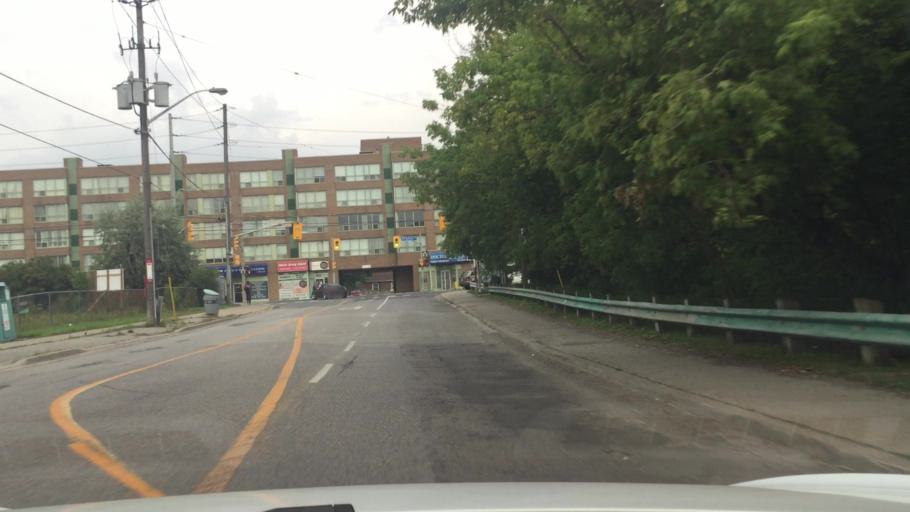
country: CA
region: Ontario
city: Scarborough
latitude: 43.7083
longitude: -79.3119
